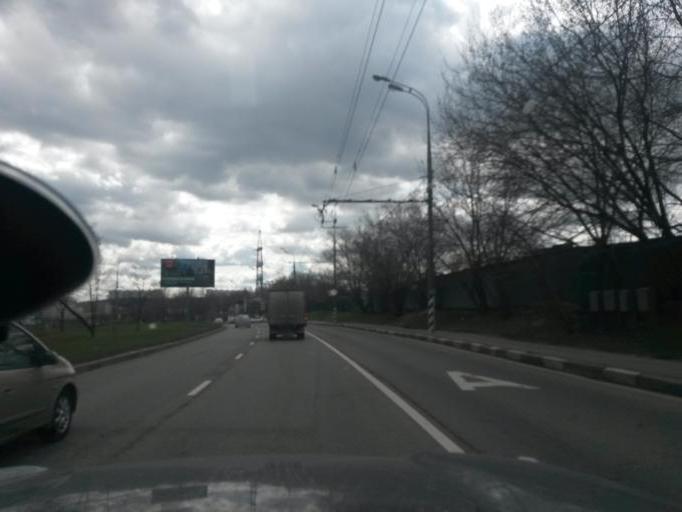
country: RU
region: Moscow
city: Yasenevo
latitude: 55.6331
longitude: 37.5403
